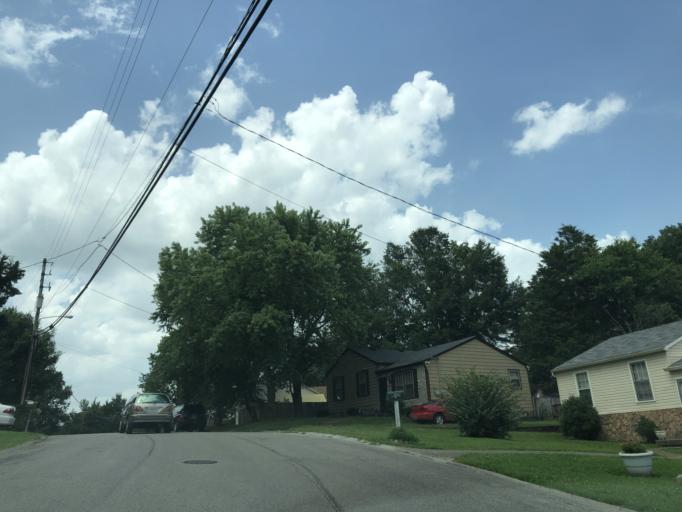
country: US
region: Tennessee
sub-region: Davidson County
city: Oak Hill
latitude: 36.0625
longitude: -86.6893
